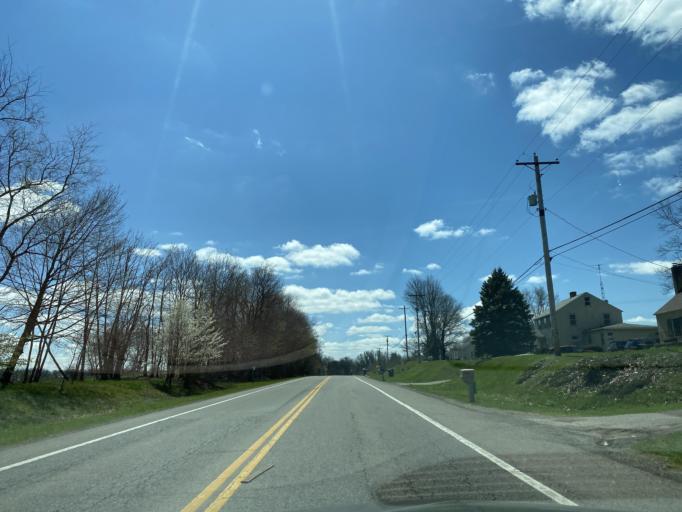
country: US
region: Ohio
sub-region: Wayne County
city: Wooster
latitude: 40.7688
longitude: -81.9728
